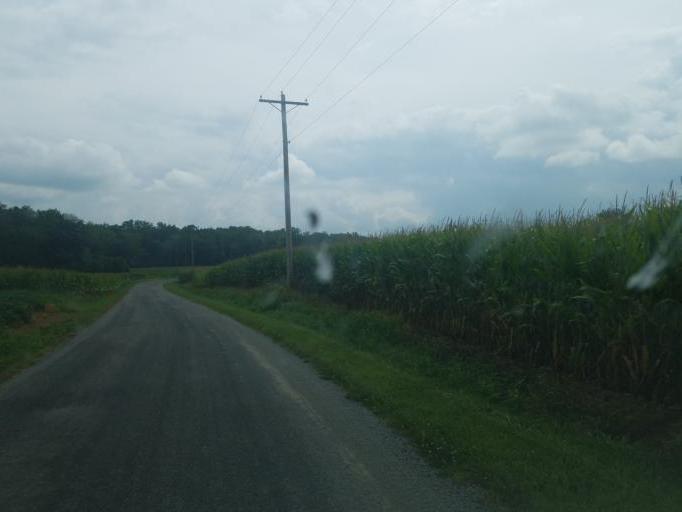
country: US
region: Ohio
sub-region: Knox County
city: Danville
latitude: 40.4819
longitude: -82.2880
